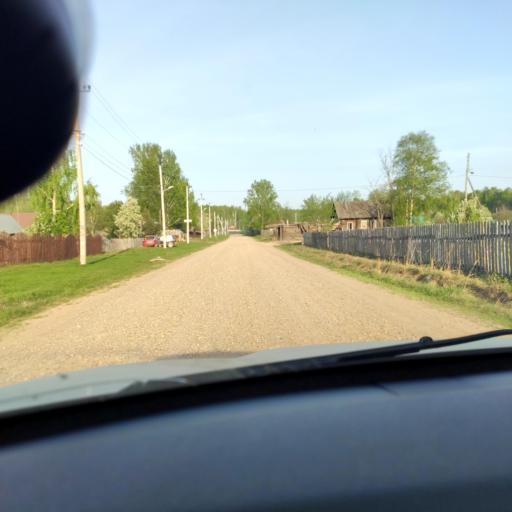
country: RU
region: Perm
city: Chermoz
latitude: 58.5996
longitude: 56.1054
